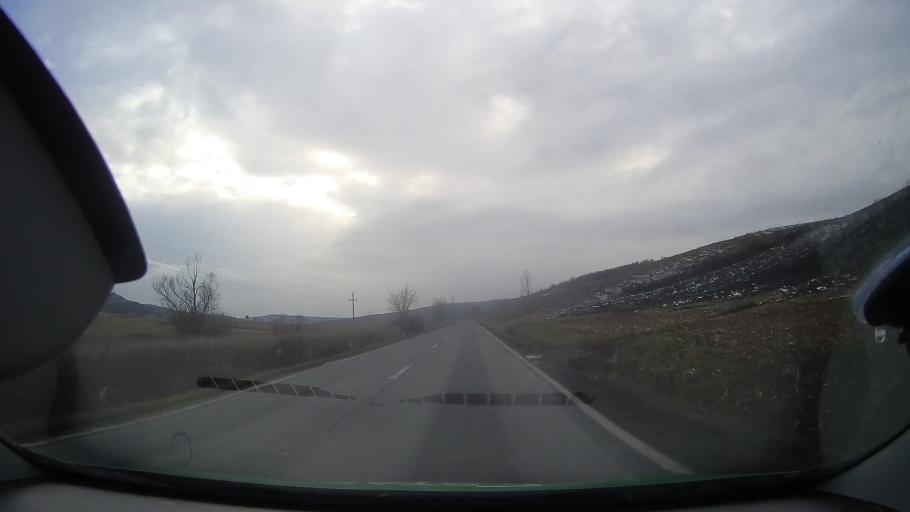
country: RO
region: Mures
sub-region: Comuna Cucerdea
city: Cucerdea
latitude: 46.3916
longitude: 24.2571
